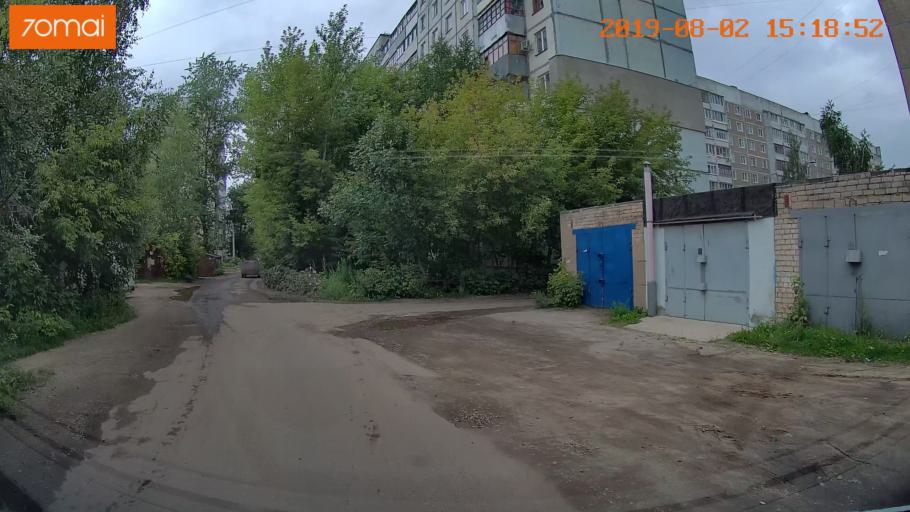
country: RU
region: Ivanovo
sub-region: Gorod Ivanovo
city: Ivanovo
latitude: 56.9800
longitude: 40.9731
